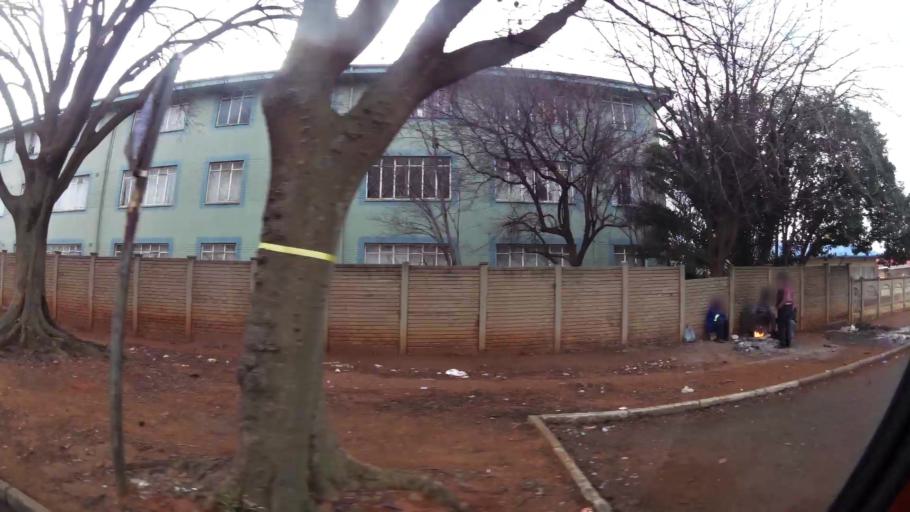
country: ZA
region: Gauteng
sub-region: Sedibeng District Municipality
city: Vanderbijlpark
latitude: -26.6959
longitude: 27.8222
